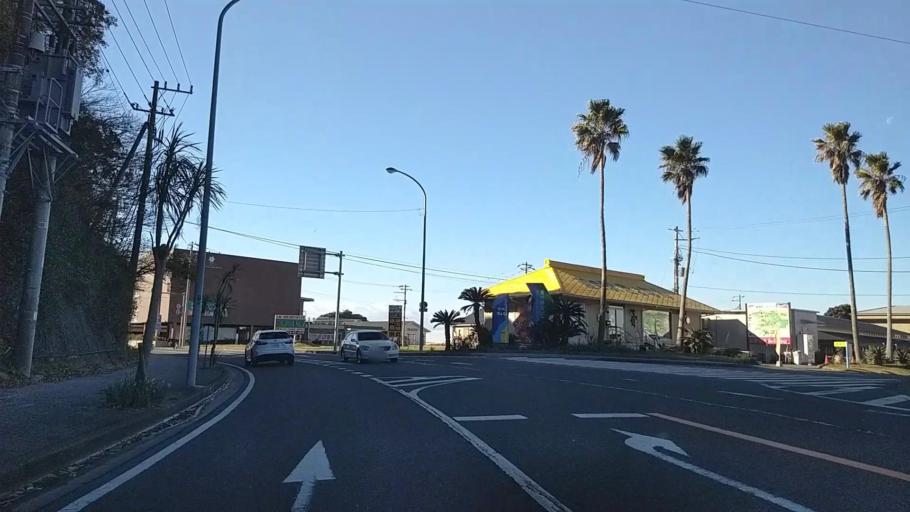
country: JP
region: Chiba
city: Tateyama
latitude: 35.1280
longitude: 139.8376
